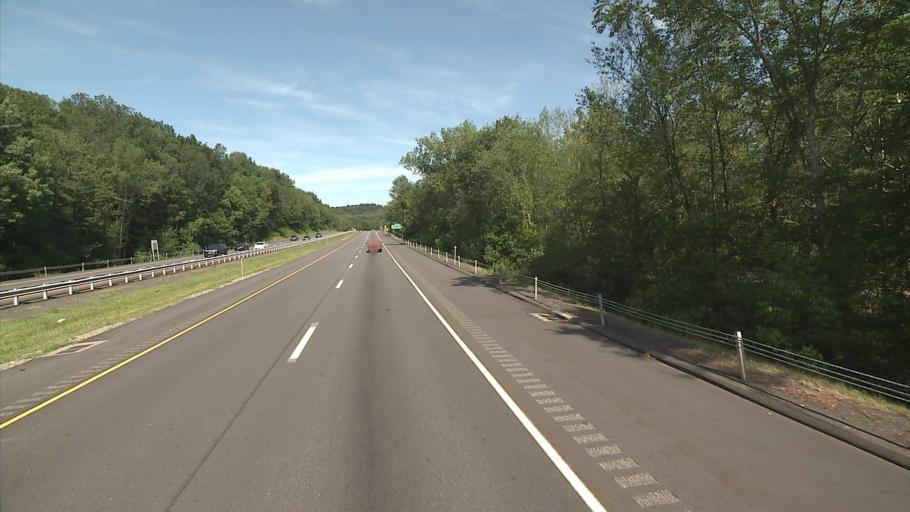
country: US
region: Connecticut
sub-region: Hartford County
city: Terramuggus
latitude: 41.6062
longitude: -72.4256
